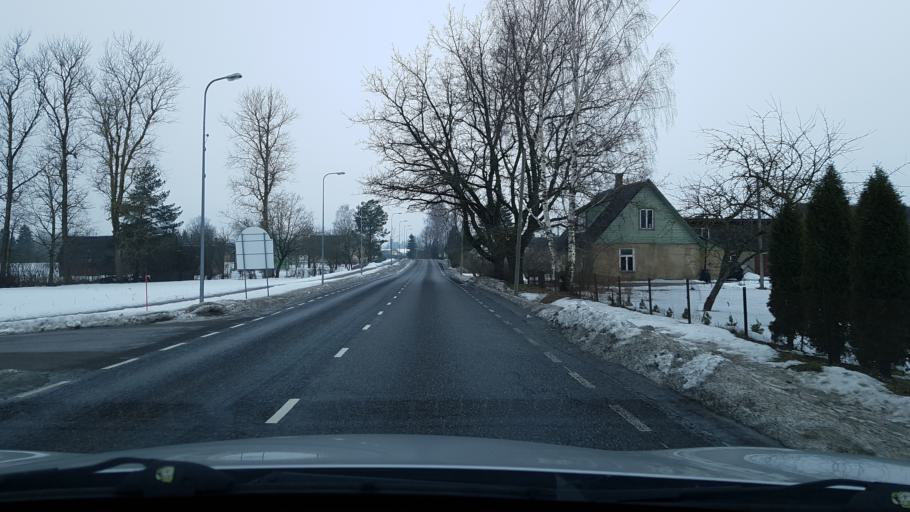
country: EE
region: Vorumaa
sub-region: Antsla vald
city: Vana-Antsla
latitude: 57.9253
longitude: 26.3261
